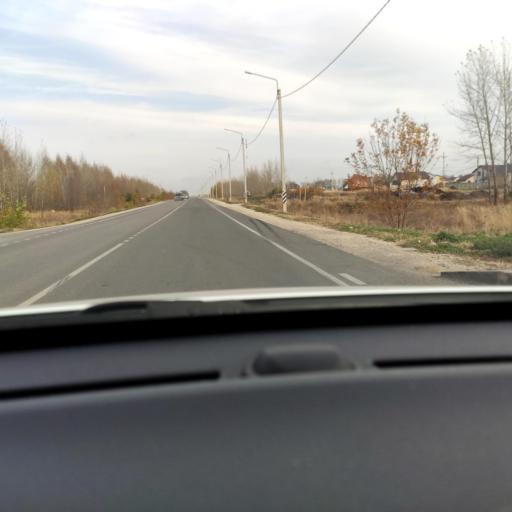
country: RU
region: Voronezj
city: Novaya Usman'
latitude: 51.6656
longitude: 39.4503
